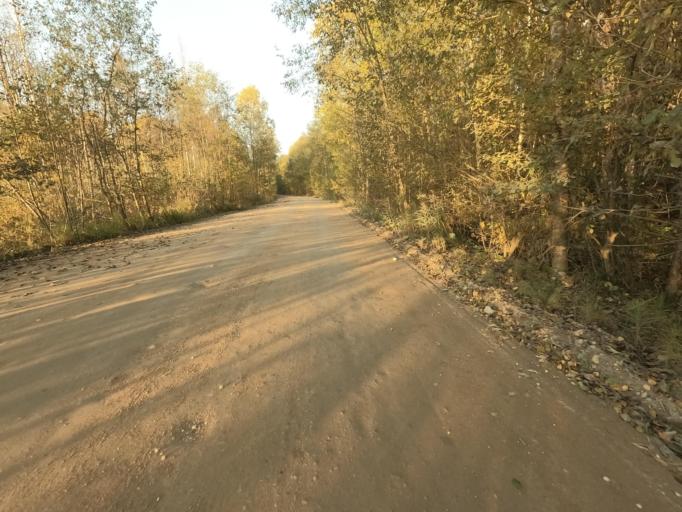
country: RU
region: Leningrad
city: Lyuban'
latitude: 58.9911
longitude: 31.1043
